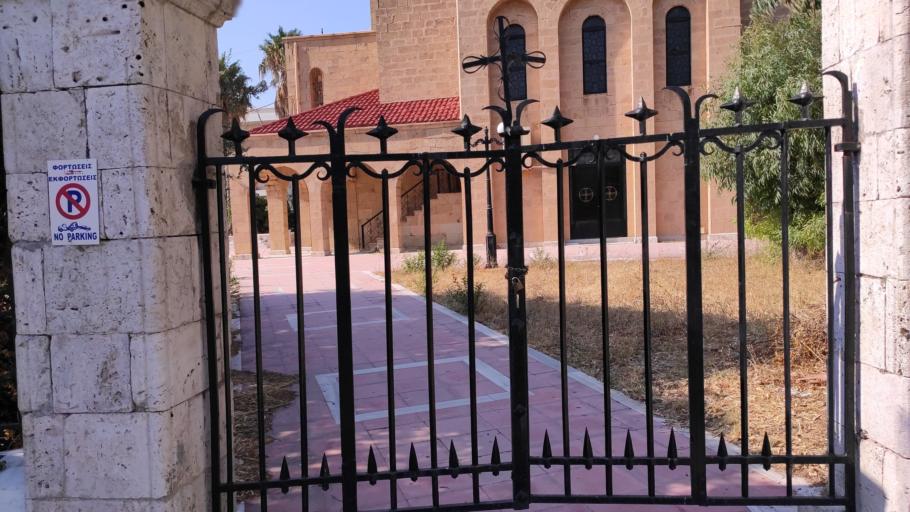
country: GR
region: South Aegean
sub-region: Nomos Dodekanisou
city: Kos
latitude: 36.8913
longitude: 27.2920
